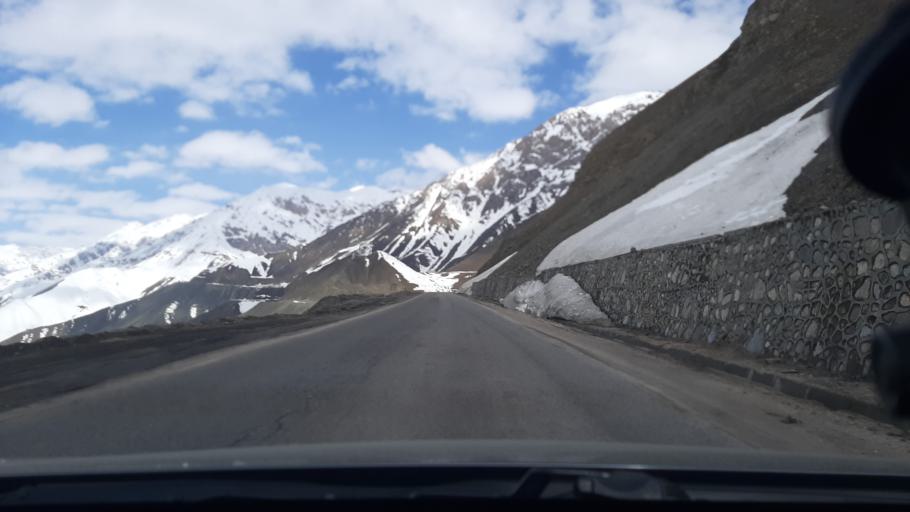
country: TJ
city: Tagob
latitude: 39.0533
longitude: 68.7367
